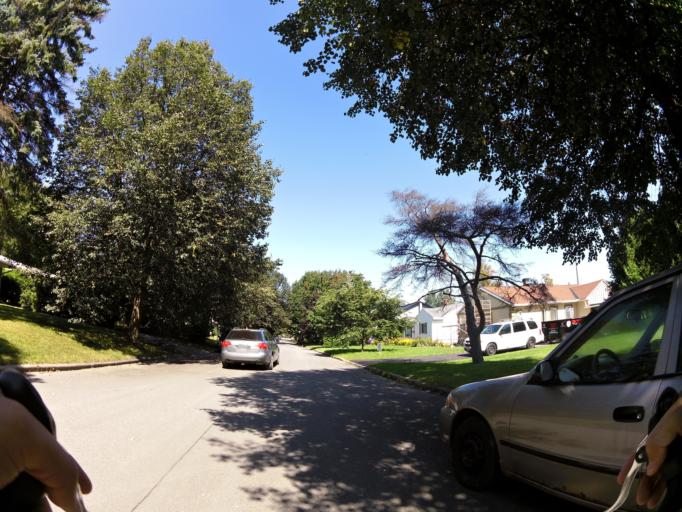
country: CA
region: Ontario
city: Ottawa
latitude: 45.3846
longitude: -75.6604
